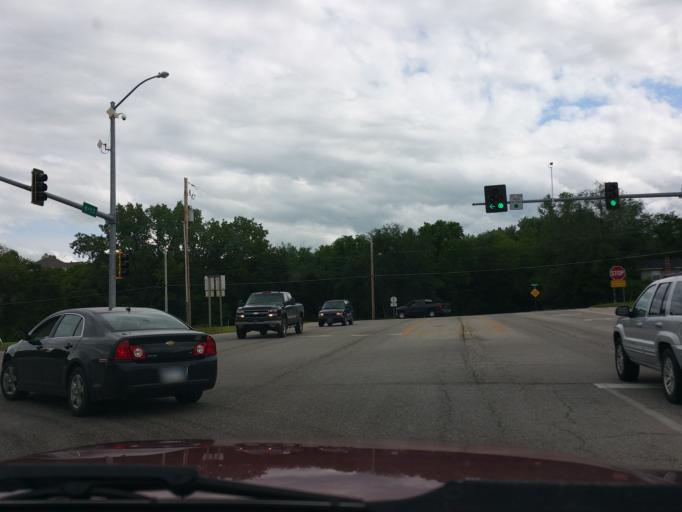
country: US
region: Kansas
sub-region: Riley County
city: Manhattan
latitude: 39.1680
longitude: -96.6038
